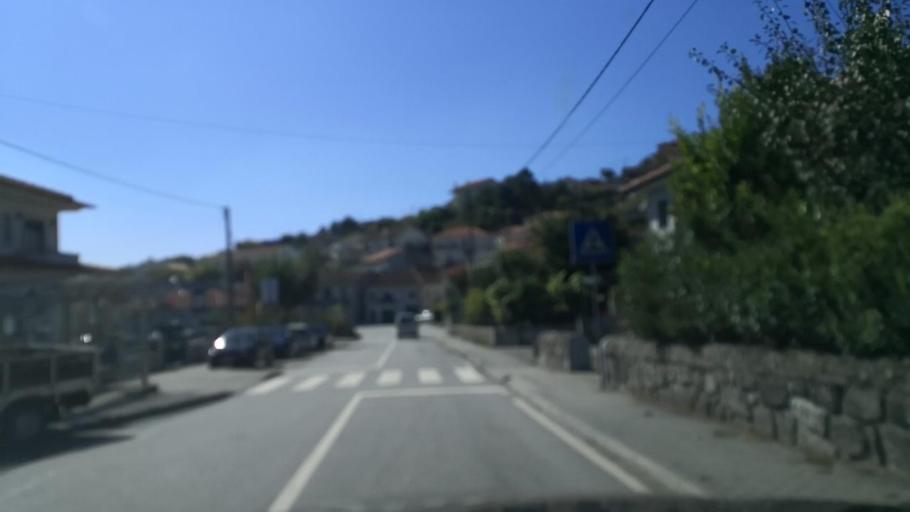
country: PT
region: Braga
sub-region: Fafe
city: Fafe
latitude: 41.4804
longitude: -8.1134
